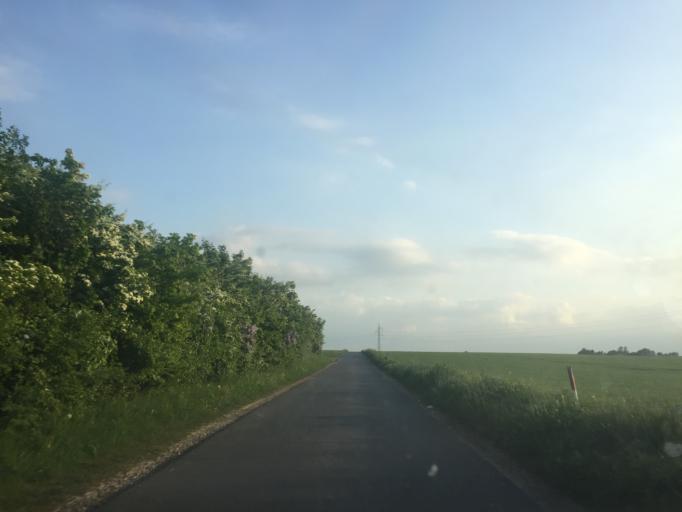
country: DK
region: South Denmark
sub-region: Kerteminde Kommune
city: Langeskov
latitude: 55.3445
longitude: 10.5211
